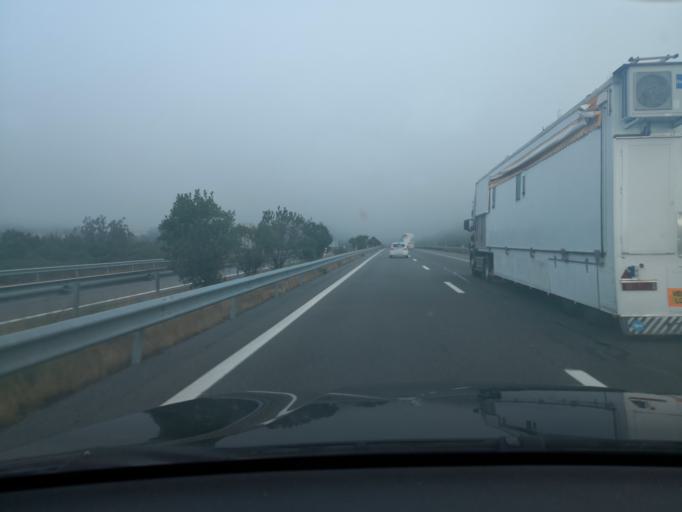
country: PT
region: Braga
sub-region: Fafe
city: Fafe
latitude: 41.4452
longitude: -8.0778
